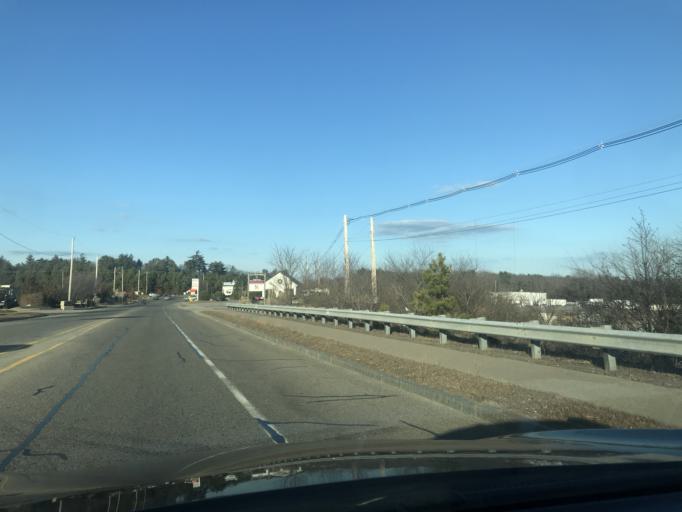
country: US
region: Massachusetts
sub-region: Plymouth County
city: North Plymouth
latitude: 41.9620
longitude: -70.7092
